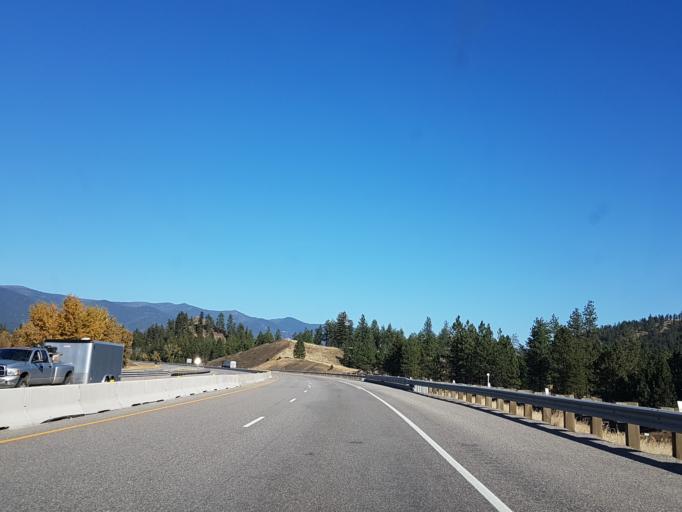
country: US
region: Montana
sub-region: Missoula County
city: Frenchtown
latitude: 47.0191
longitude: -114.3684
